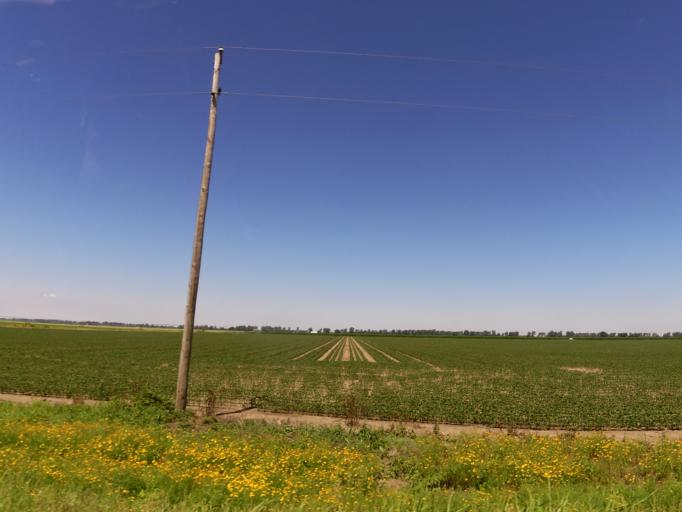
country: US
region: Missouri
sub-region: New Madrid County
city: Lilbourn
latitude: 36.5692
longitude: -89.7029
